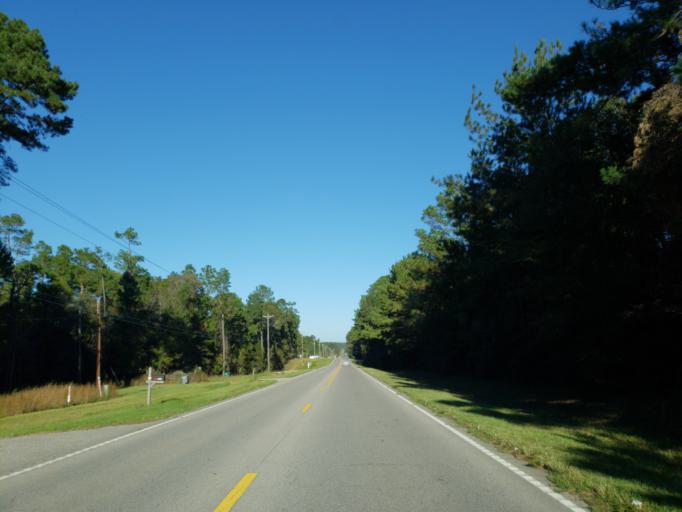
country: US
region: Mississippi
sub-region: Forrest County
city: Petal
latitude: 31.3607
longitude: -89.1521
